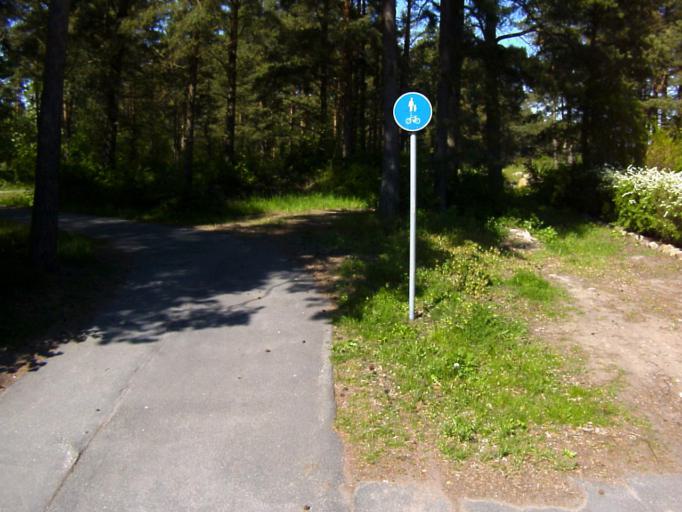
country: SE
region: Skane
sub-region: Kristianstads Kommun
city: Degeberga
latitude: 55.9010
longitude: 14.1028
